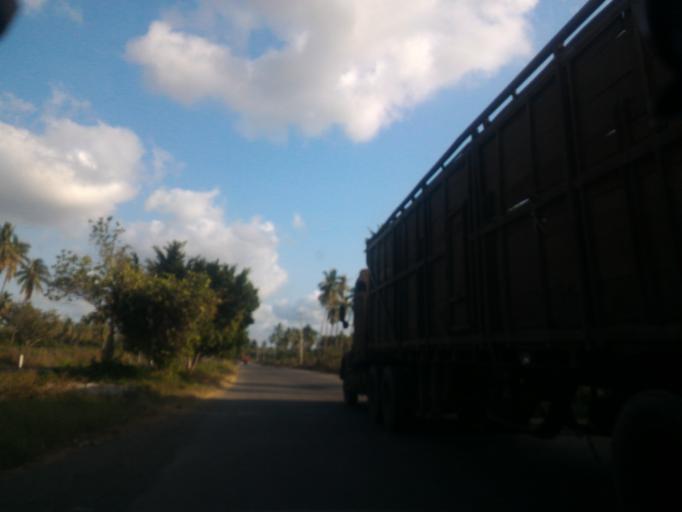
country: MX
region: Colima
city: Tecoman
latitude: 18.9283
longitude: -103.8573
